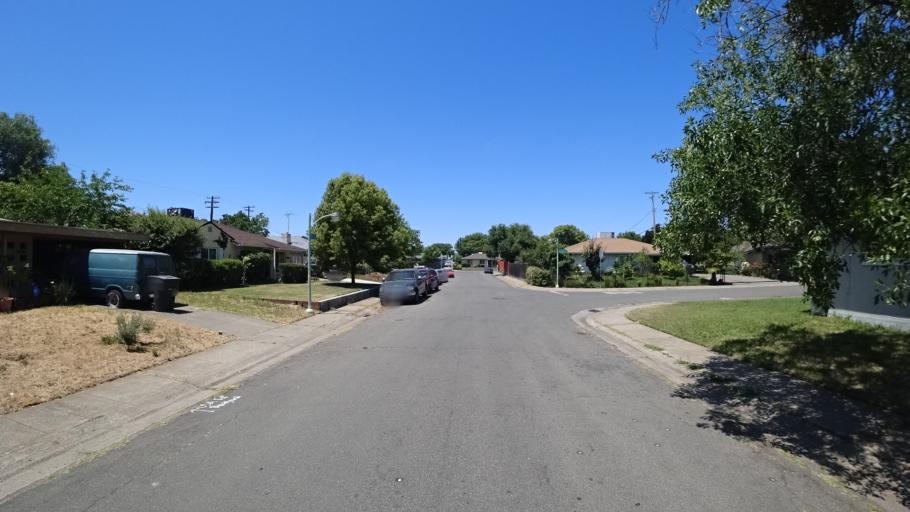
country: US
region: California
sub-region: Sacramento County
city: Florin
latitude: 38.5262
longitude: -121.4318
